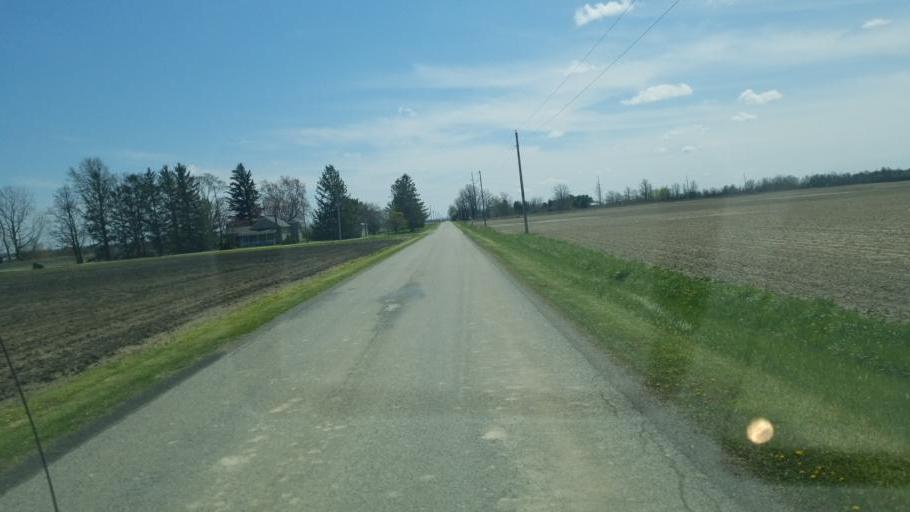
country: US
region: Ohio
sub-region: Union County
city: Richwood
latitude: 40.4820
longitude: -83.2578
